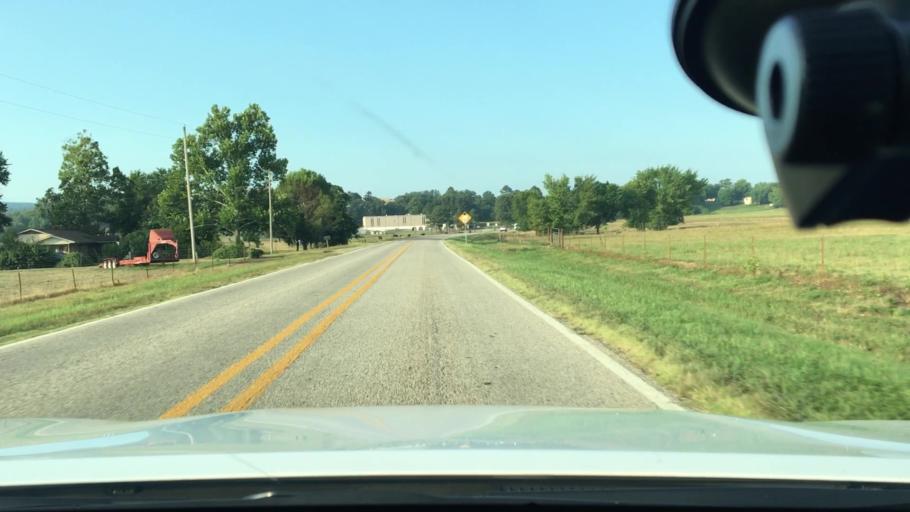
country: US
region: Arkansas
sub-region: Logan County
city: Paris
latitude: 35.3063
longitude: -93.6331
